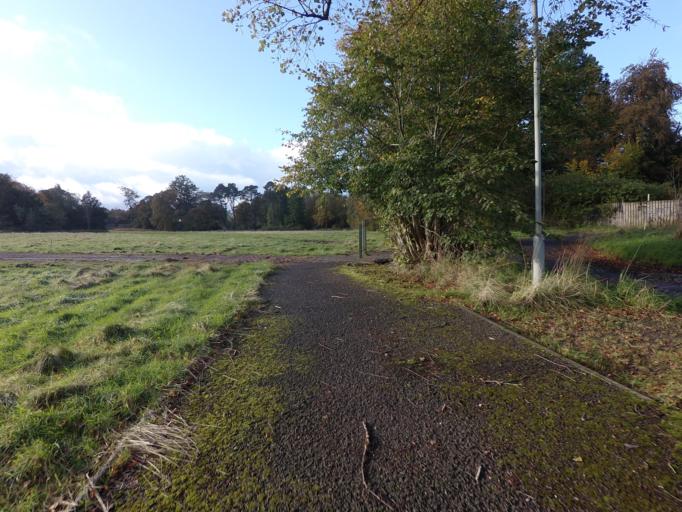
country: GB
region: Scotland
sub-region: West Lothian
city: West Calder
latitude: 55.8624
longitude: -3.5419
